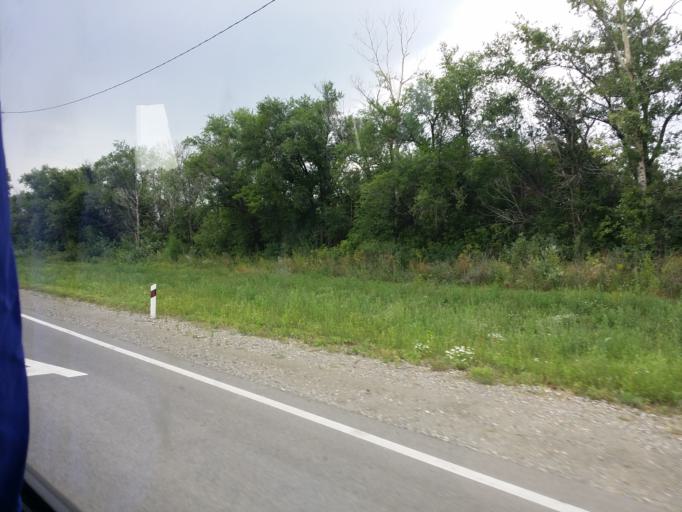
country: RU
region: Altai Krai
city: Malougrenevo
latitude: 52.5774
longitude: 85.3001
